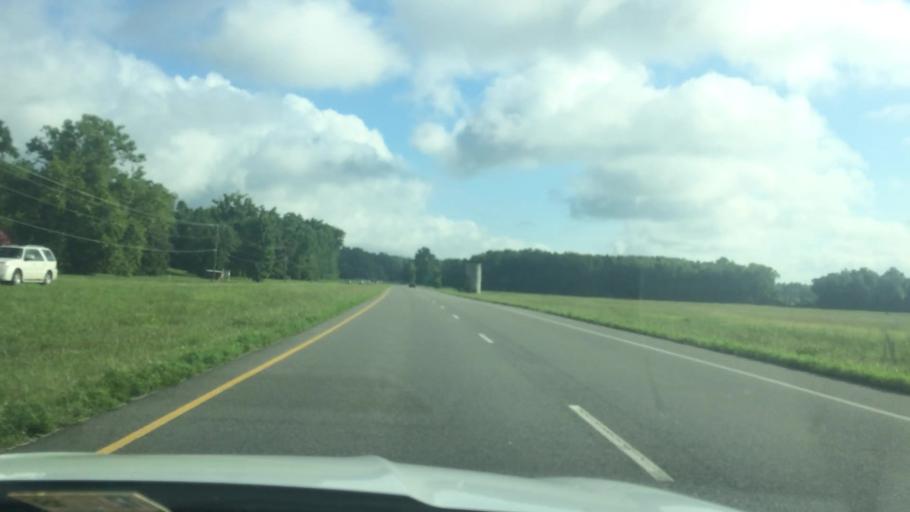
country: US
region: Virginia
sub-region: Gloucester County
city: Gloucester Courthouse
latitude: 37.4407
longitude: -76.4755
